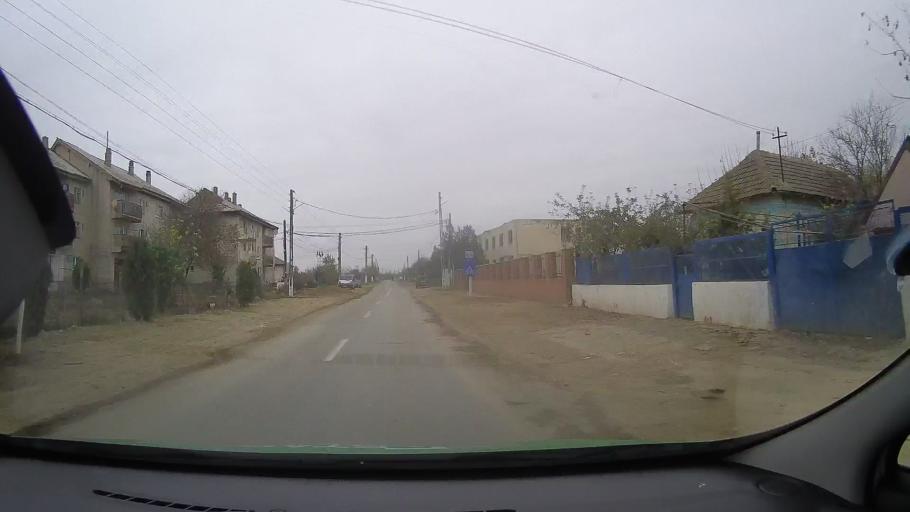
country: RO
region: Constanta
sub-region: Comuna Vulturu
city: Vulturu
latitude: 44.6482
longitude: 28.2693
